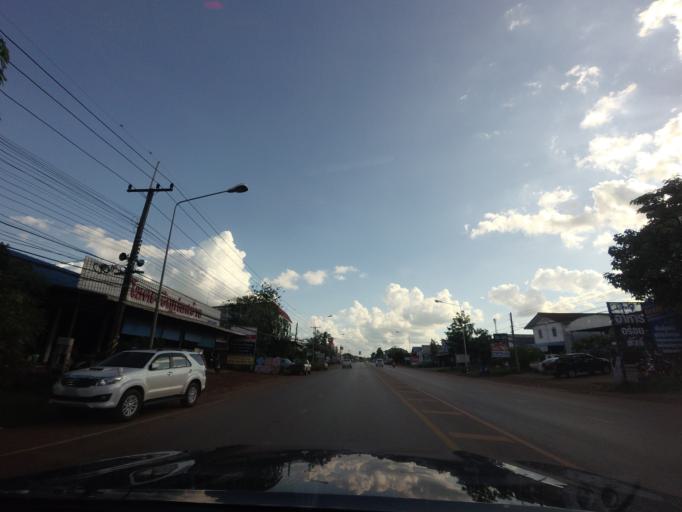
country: TH
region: Changwat Udon Thani
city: Ban Dung
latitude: 17.6848
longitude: 103.2559
